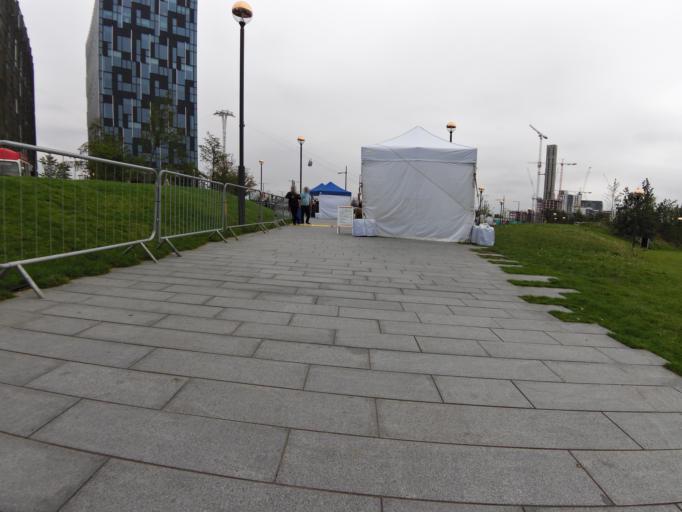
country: GB
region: England
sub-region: Greater London
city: Poplar
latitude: 51.5006
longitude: 0.0054
